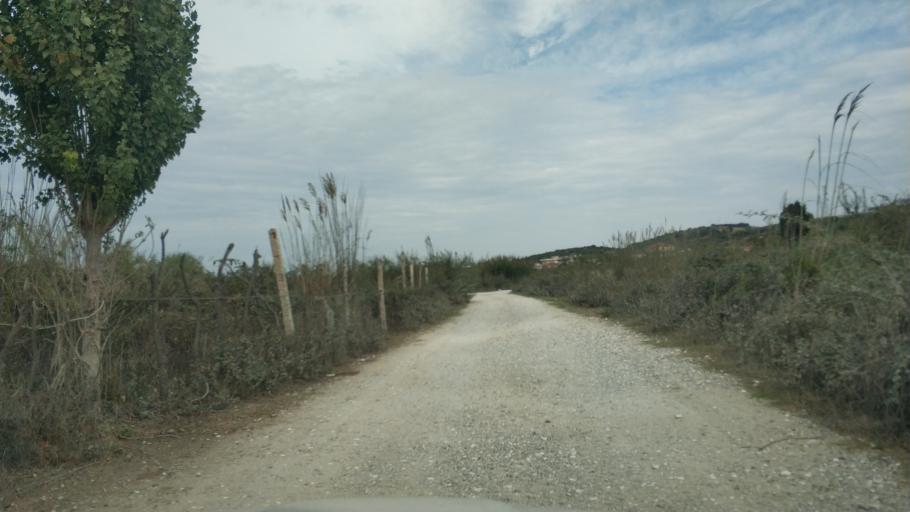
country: AL
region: Vlore
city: Vlore
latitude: 40.5047
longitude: 19.4093
